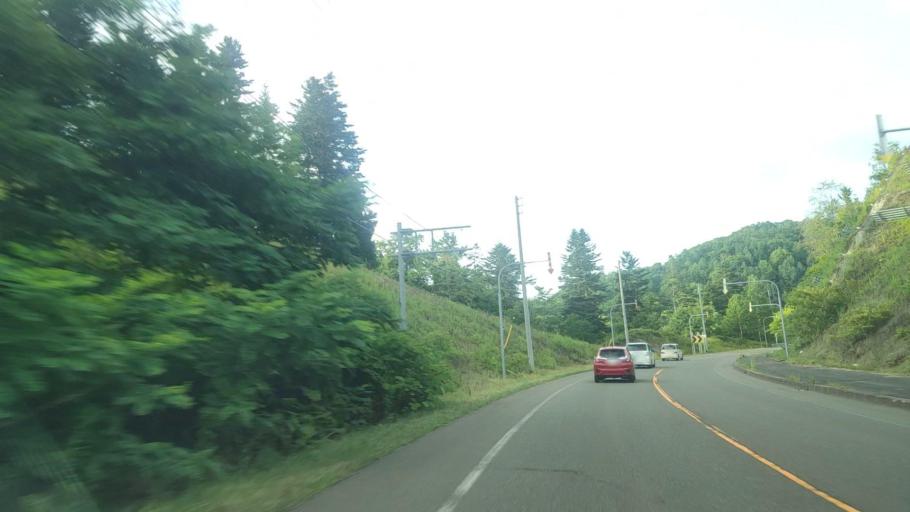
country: JP
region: Hokkaido
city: Iwamizawa
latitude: 43.0265
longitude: 141.9537
